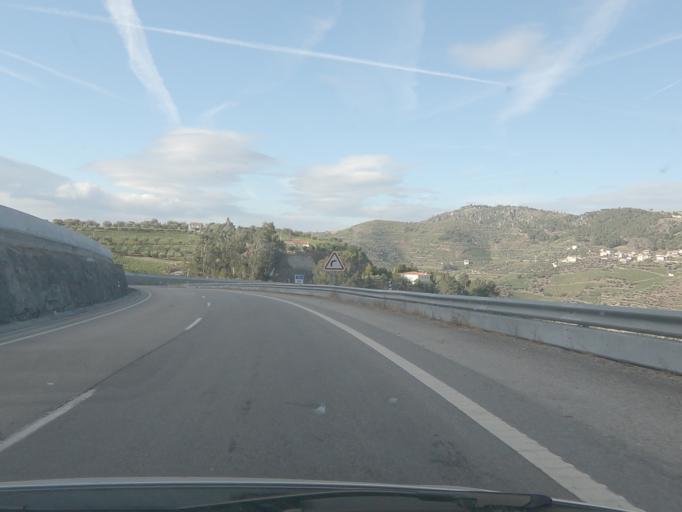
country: PT
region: Viseu
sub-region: Lamego
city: Lamego
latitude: 41.0976
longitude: -7.7808
